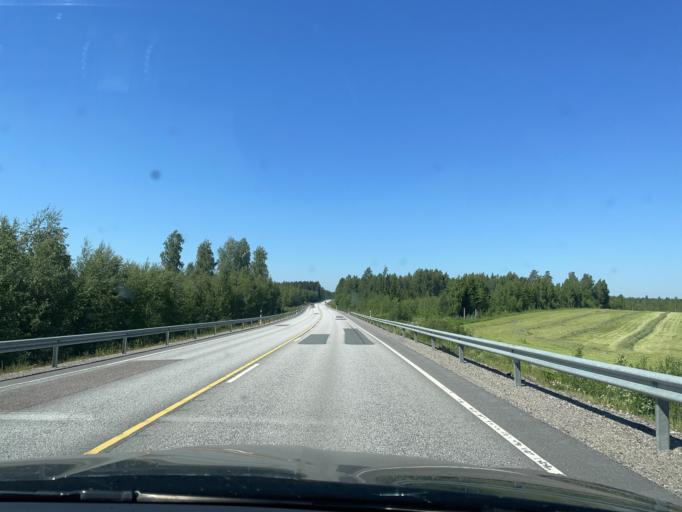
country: FI
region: Central Finland
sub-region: Saarijaervi-Viitasaari
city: Viitasaari
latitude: 63.1425
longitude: 25.8288
